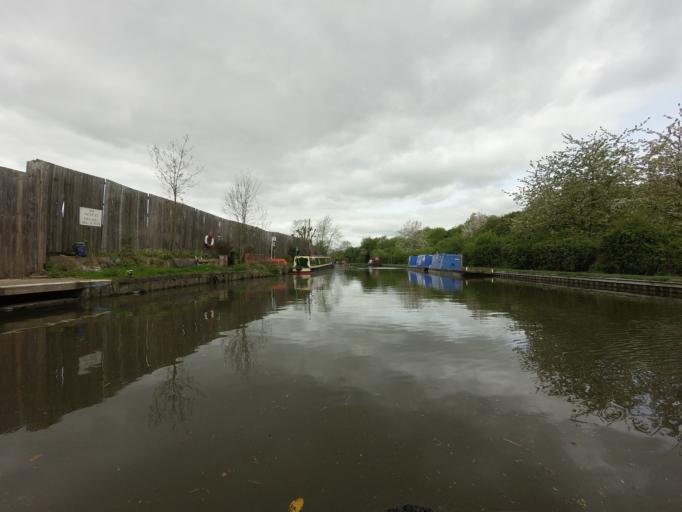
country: GB
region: England
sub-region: Milton Keynes
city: Water Eaton
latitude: 52.0012
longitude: -0.7145
